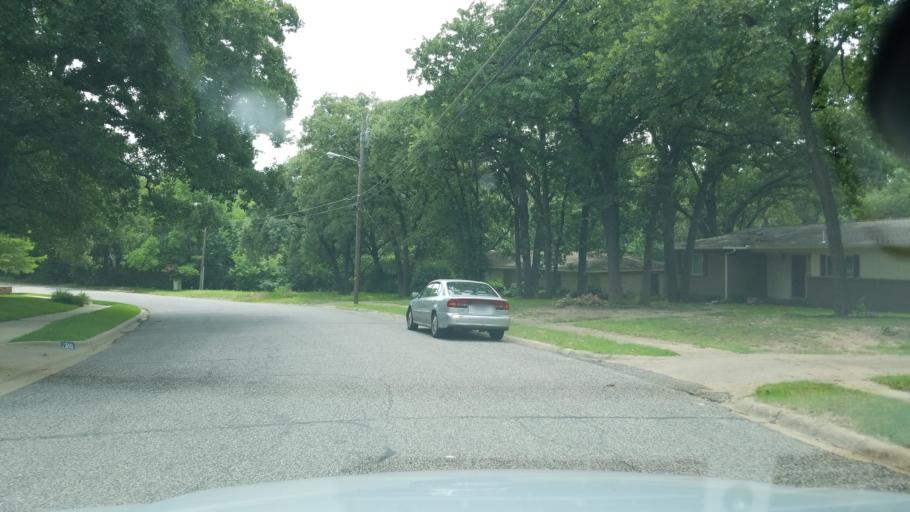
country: US
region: Texas
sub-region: Dallas County
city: Irving
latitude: 32.8284
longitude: -96.9245
